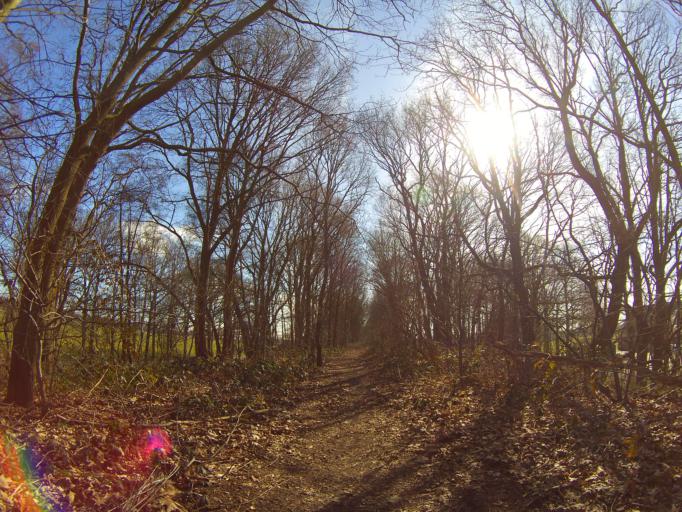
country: NL
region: Utrecht
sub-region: Gemeente Utrechtse Heuvelrug
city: Overberg
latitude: 52.0599
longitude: 5.4688
